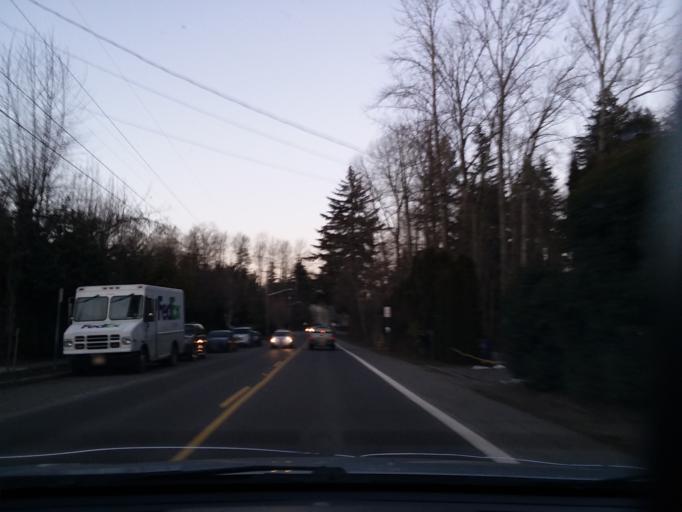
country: US
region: Washington
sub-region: Snohomish County
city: Martha Lake
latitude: 47.8800
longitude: -122.2589
